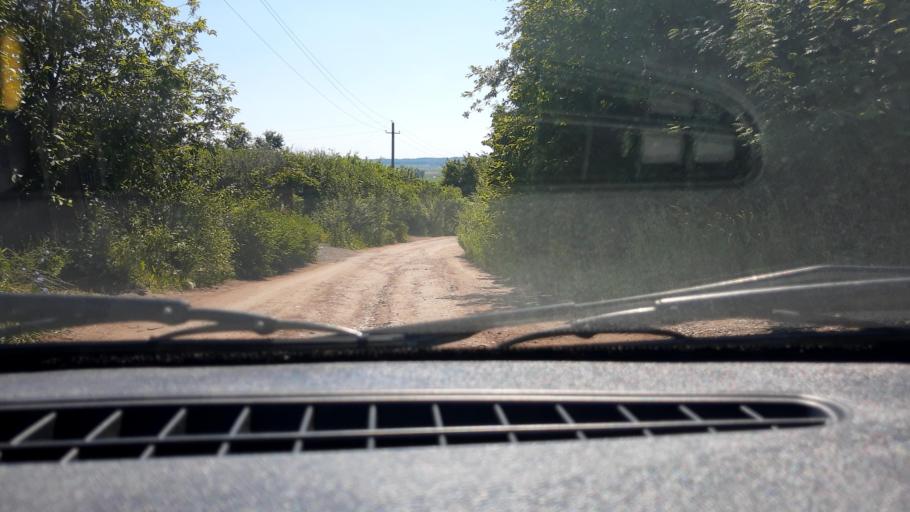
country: RU
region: Bashkortostan
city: Karmaskaly
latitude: 54.3625
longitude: 55.8931
